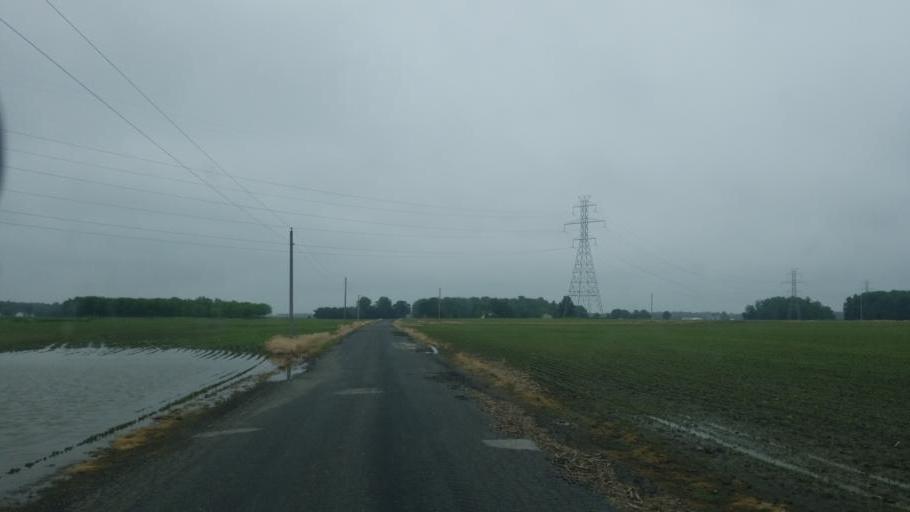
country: US
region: Indiana
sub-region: Marshall County
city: Bremen
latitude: 41.4794
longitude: -86.1298
